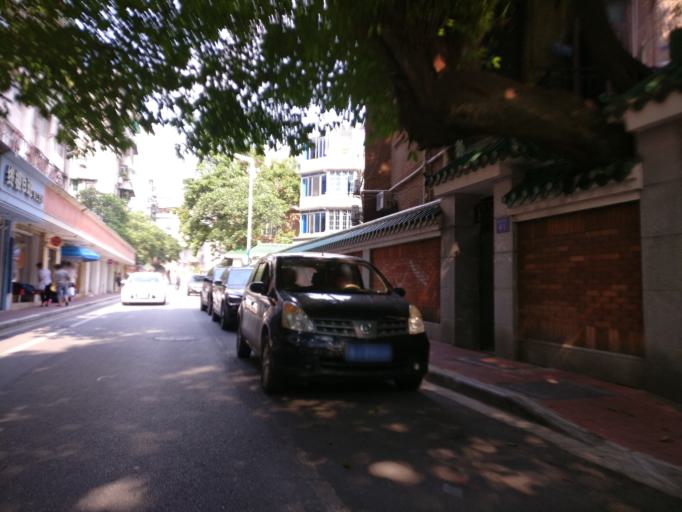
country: CN
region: Guangdong
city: Guangzhou
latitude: 23.1245
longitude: 113.2866
